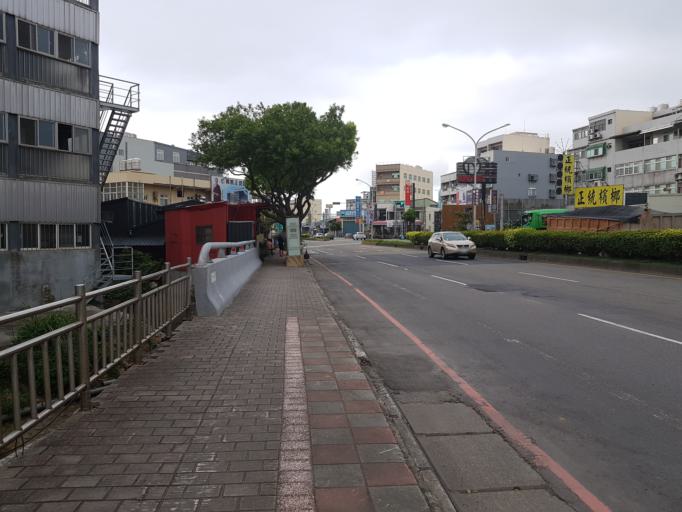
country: TW
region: Taiwan
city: Taoyuan City
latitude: 25.0741
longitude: 121.2603
